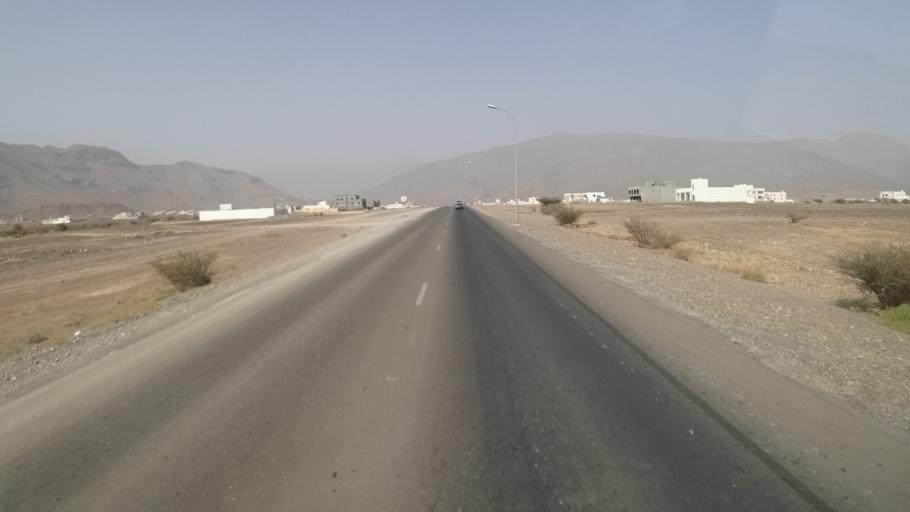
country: OM
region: Muhafazat ad Dakhiliyah
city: Nizwa
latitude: 22.9093
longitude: 57.5843
